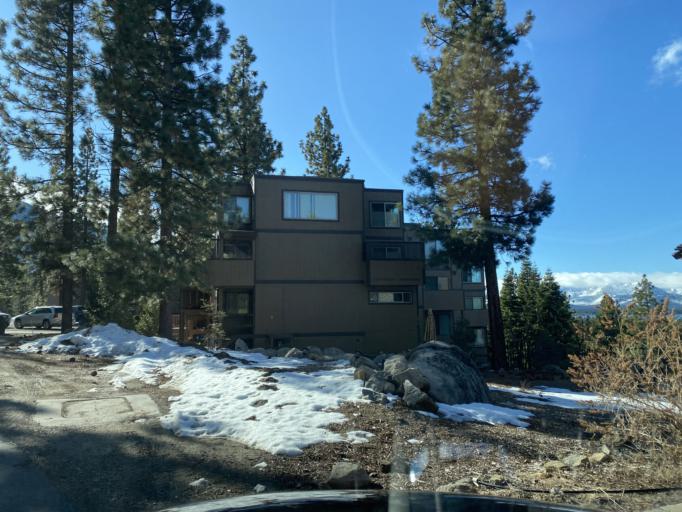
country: US
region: Nevada
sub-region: Douglas County
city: Kingsbury
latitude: 38.9785
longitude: -119.9339
